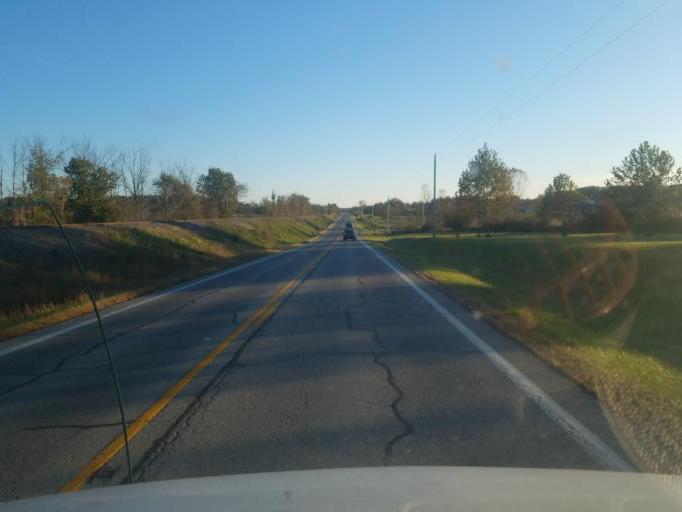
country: US
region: Ohio
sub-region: Licking County
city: Utica
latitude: 40.2658
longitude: -82.4506
